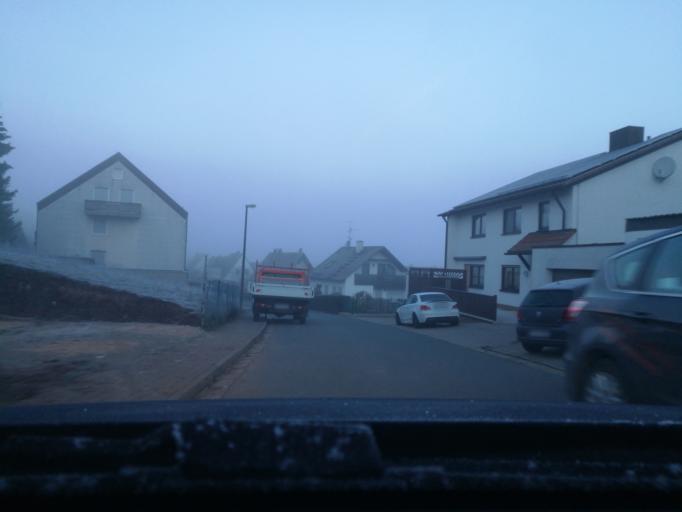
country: DE
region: Bavaria
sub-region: Regierungsbezirk Mittelfranken
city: Veitsbronn
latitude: 49.5054
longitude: 10.8892
